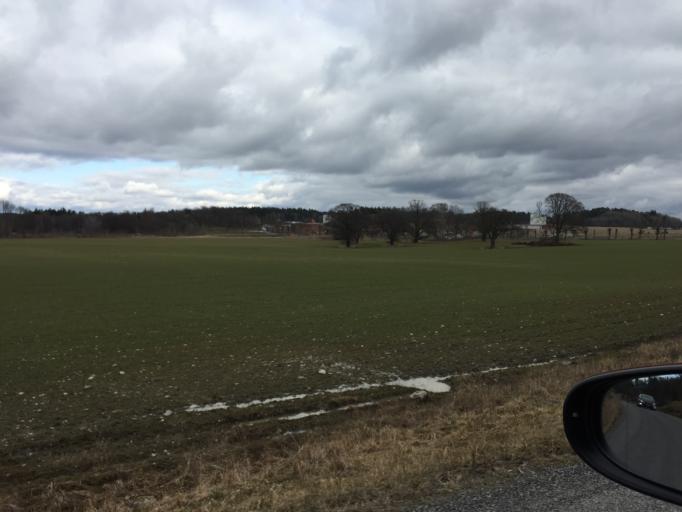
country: SE
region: Stockholm
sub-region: Botkyrka Kommun
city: Eriksberg
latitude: 59.2481
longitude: 17.7839
